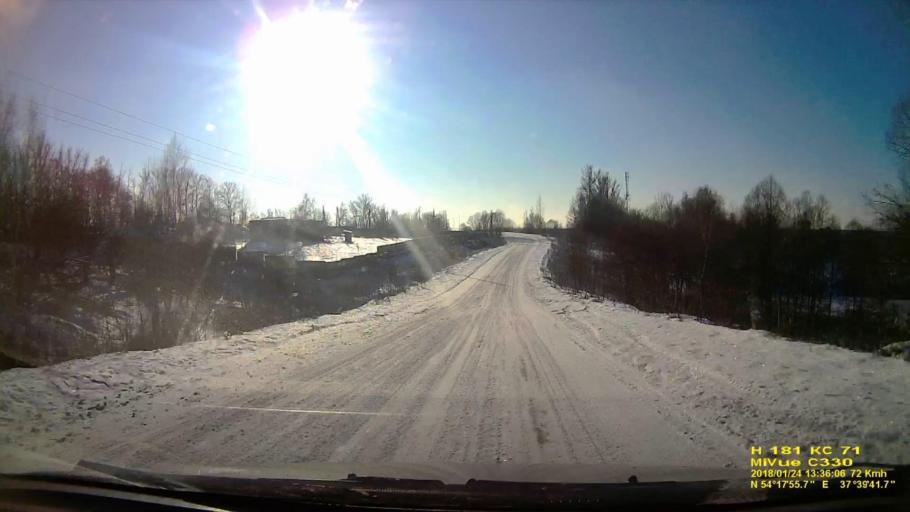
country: RU
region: Tula
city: Gorelki
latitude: 54.2987
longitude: 37.6615
